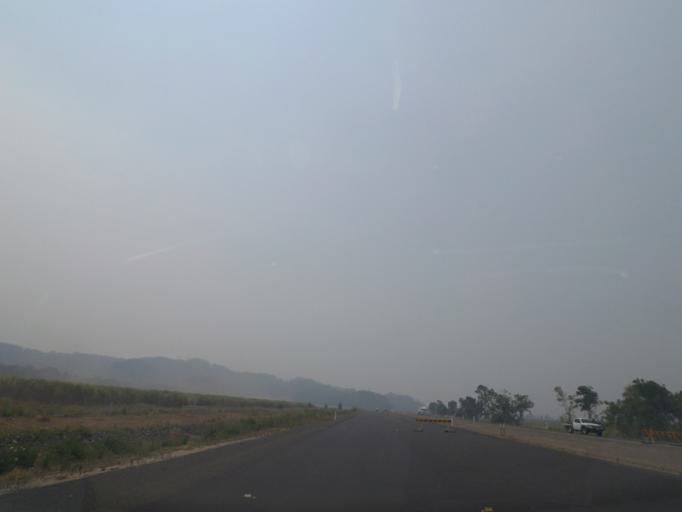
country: AU
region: New South Wales
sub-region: Ballina
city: Ballina
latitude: -28.8900
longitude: 153.4822
